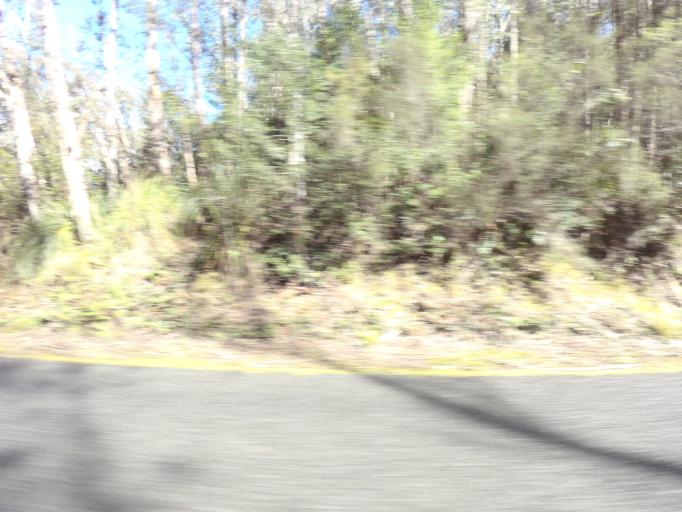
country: AU
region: Tasmania
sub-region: Derwent Valley
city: New Norfolk
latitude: -42.7507
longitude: 146.4120
